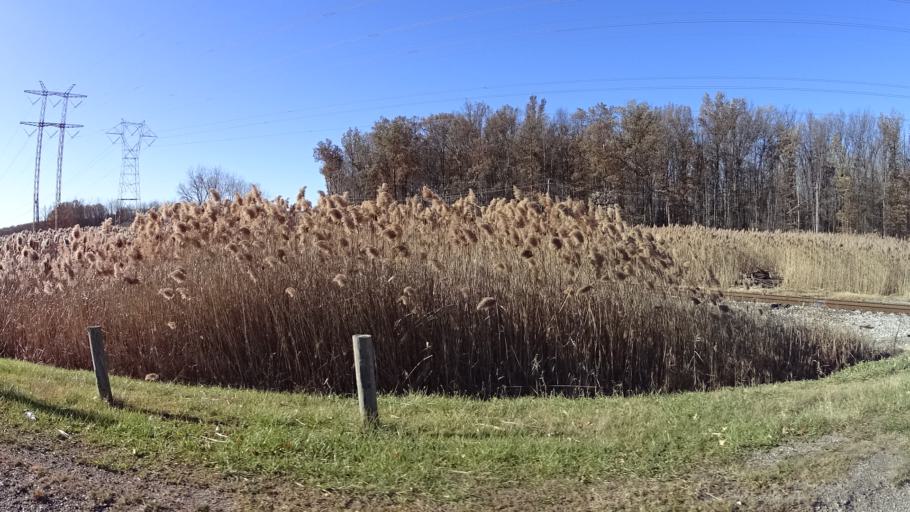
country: US
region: Ohio
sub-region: Lorain County
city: Avon
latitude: 41.4792
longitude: -82.0612
